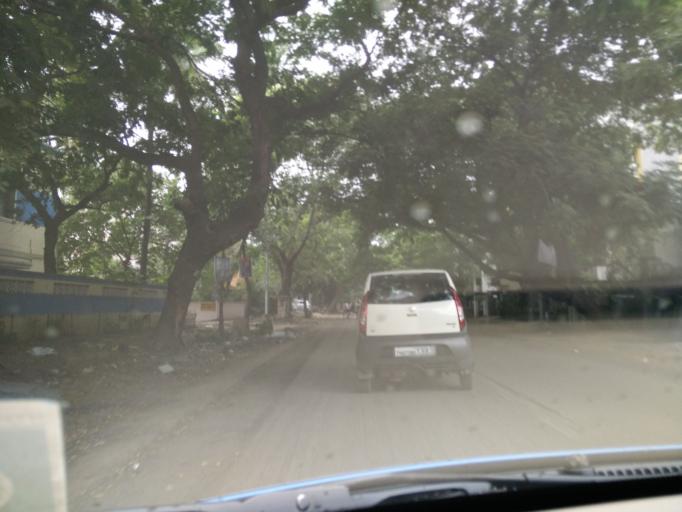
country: IN
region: Tamil Nadu
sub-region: Chennai
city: Gandhi Nagar
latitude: 12.9959
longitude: 80.2521
